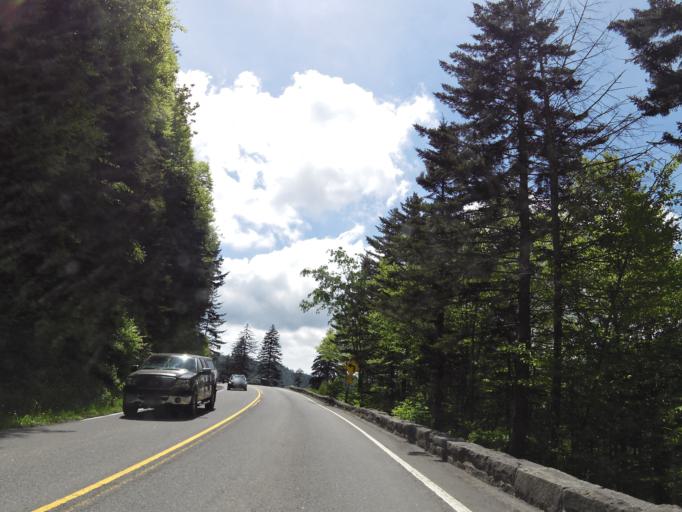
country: US
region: Tennessee
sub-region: Sevier County
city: Gatlinburg
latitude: 35.6199
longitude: -83.4196
